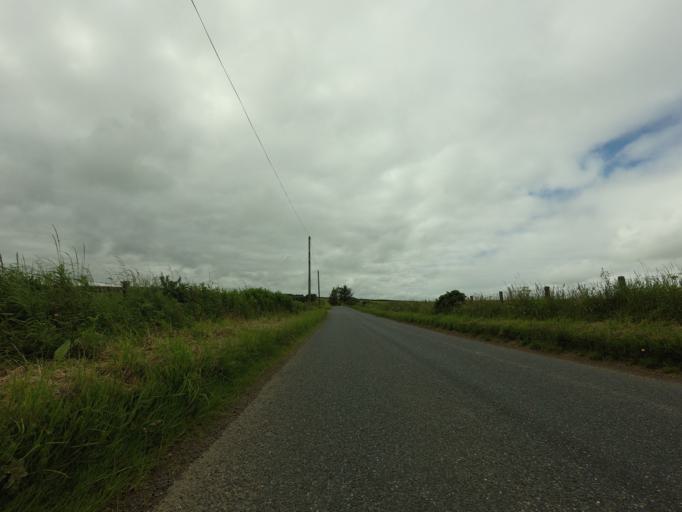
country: GB
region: Scotland
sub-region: Aberdeenshire
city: Rosehearty
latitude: 57.5419
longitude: -2.2075
